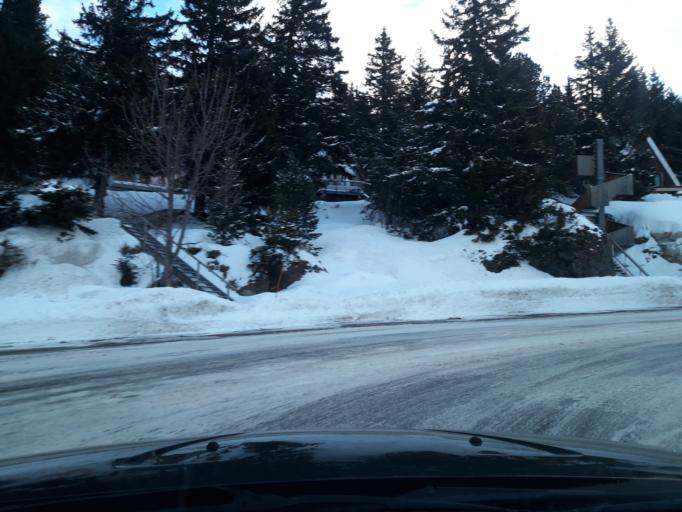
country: FR
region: Rhone-Alpes
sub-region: Departement de l'Isere
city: Vaulnaveys-le-Bas
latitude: 45.1153
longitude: 5.8761
